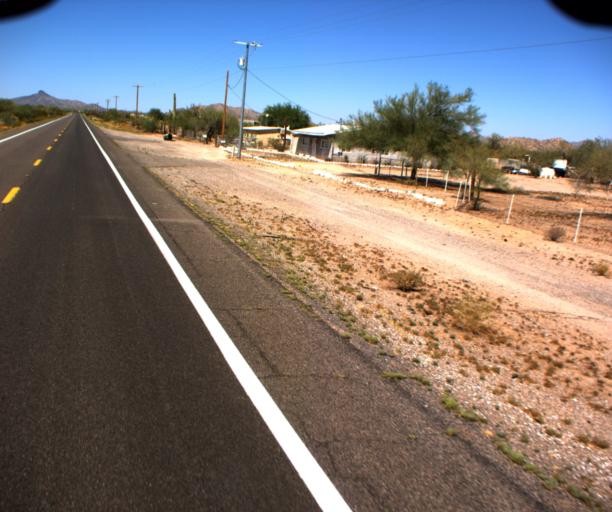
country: US
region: Arizona
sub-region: Pinal County
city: Maricopa
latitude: 32.8647
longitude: -112.0679
